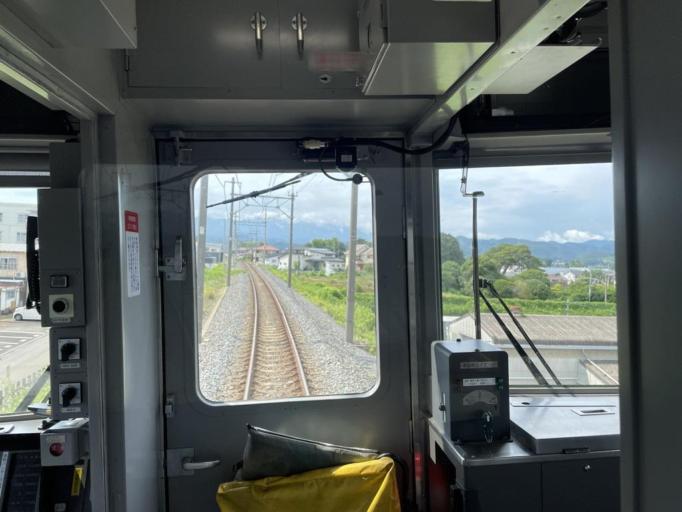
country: JP
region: Gunma
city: Kiryu
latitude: 36.4041
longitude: 139.3118
